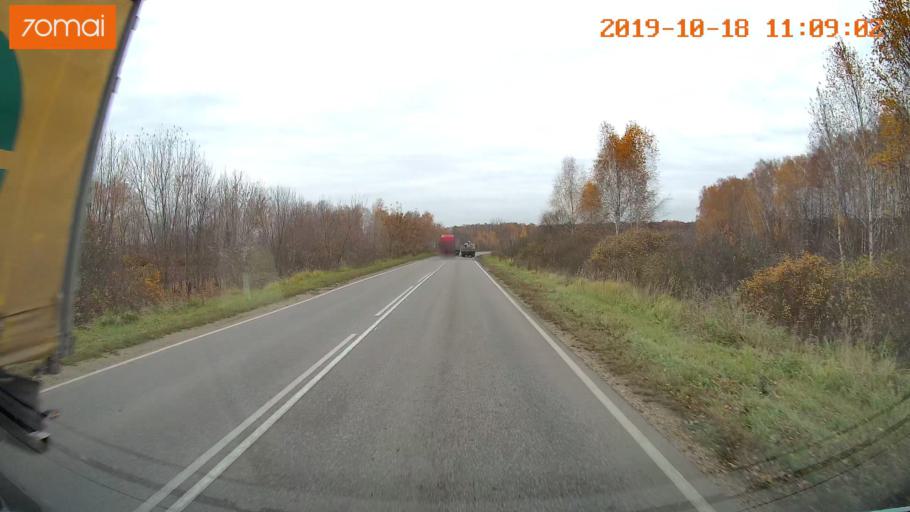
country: RU
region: Tula
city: Kimovsk
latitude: 53.9473
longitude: 38.5330
